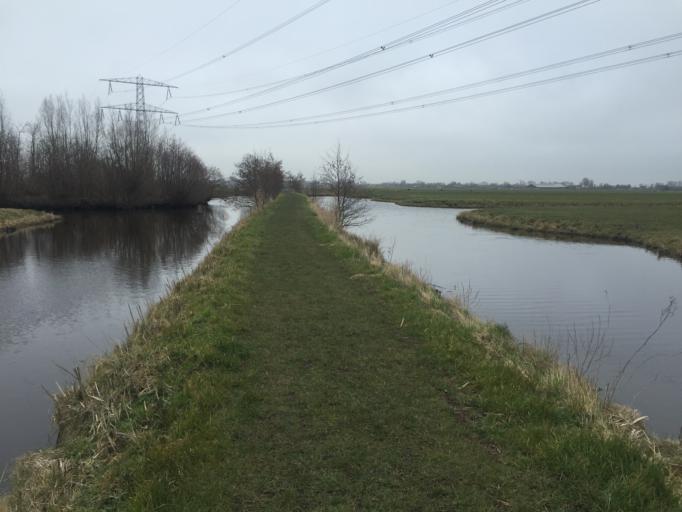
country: NL
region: South Holland
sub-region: Gemeente Vlist
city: Haastrecht
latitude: 52.0098
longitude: 4.7698
